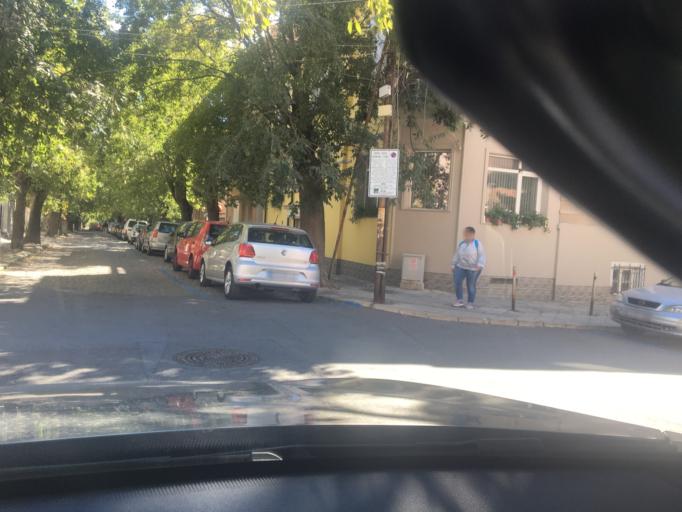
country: BG
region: Burgas
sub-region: Obshtina Burgas
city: Burgas
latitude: 42.4995
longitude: 27.4770
